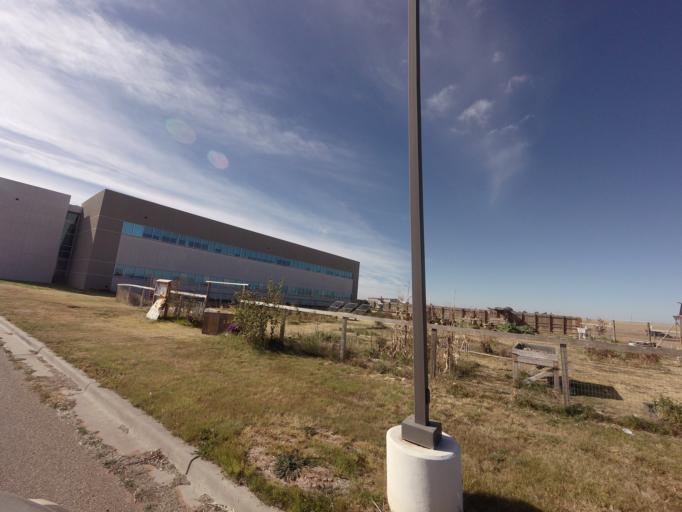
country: US
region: New Mexico
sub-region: Curry County
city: Clovis
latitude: 34.4207
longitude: -103.2358
